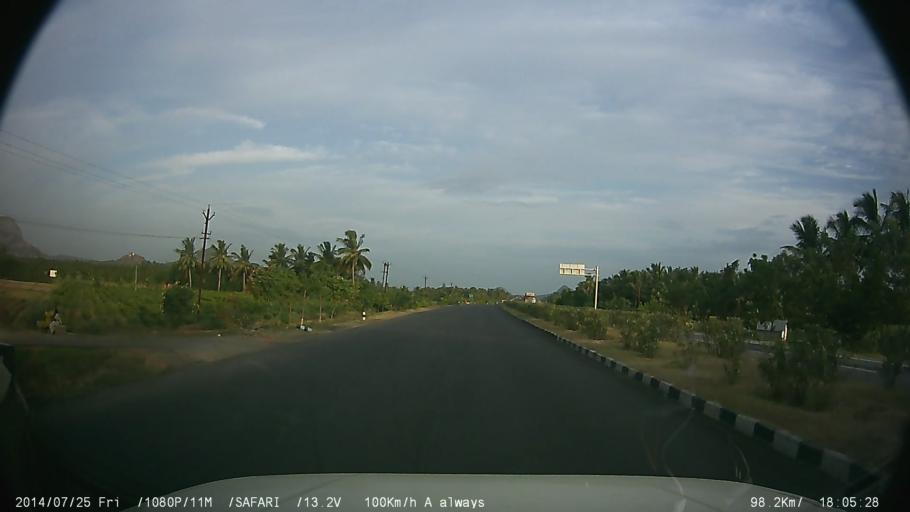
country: IN
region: Tamil Nadu
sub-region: Krishnagiri
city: Kaverippattanam
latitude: 12.4385
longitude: 78.2212
